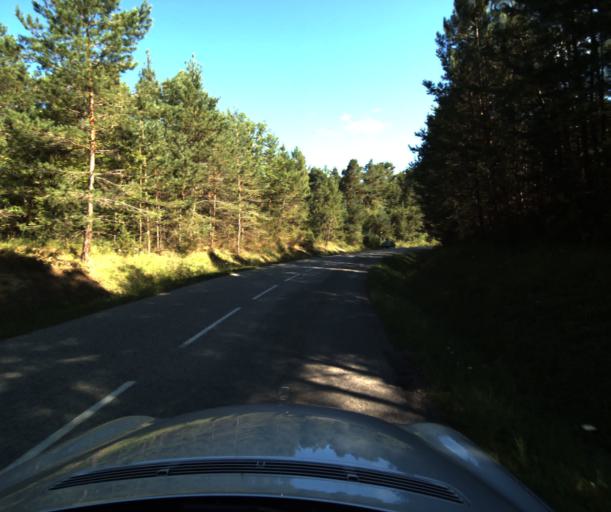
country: FR
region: Languedoc-Roussillon
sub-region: Departement de l'Aude
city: Chalabre
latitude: 42.9624
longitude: 1.9857
